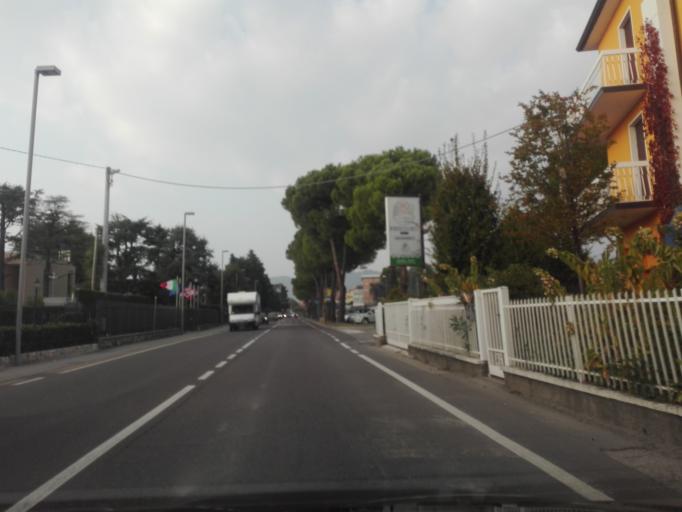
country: IT
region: Veneto
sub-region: Provincia di Verona
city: Bardolino
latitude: 45.5392
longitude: 10.7268
